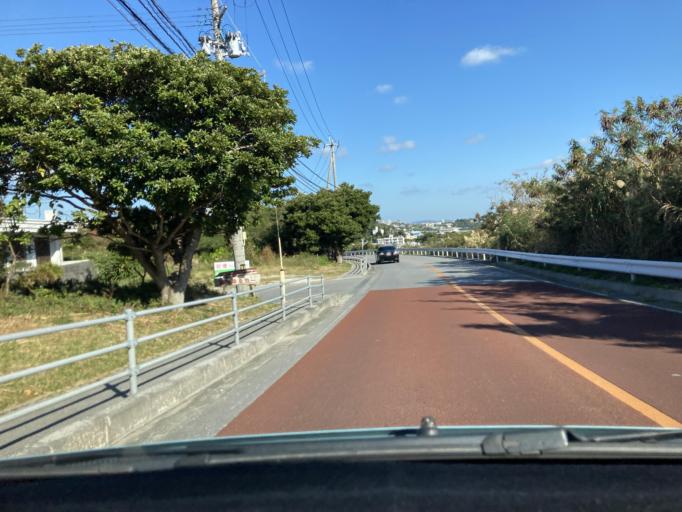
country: JP
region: Okinawa
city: Chatan
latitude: 26.2954
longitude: 127.7996
